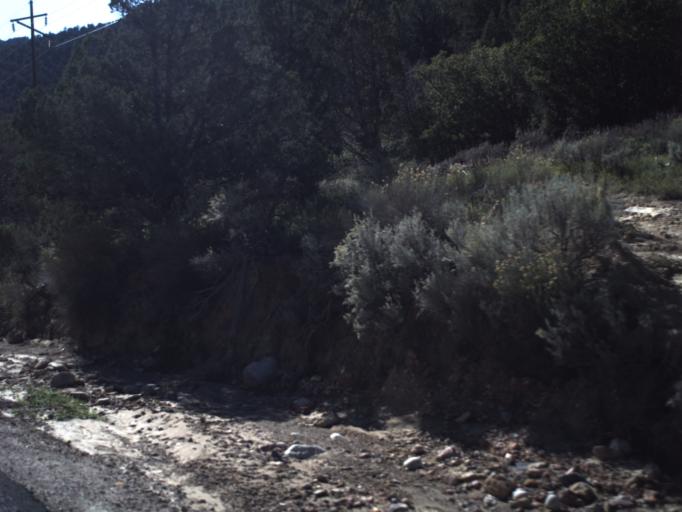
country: US
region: Utah
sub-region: Iron County
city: Parowan
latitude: 37.7920
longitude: -112.8205
